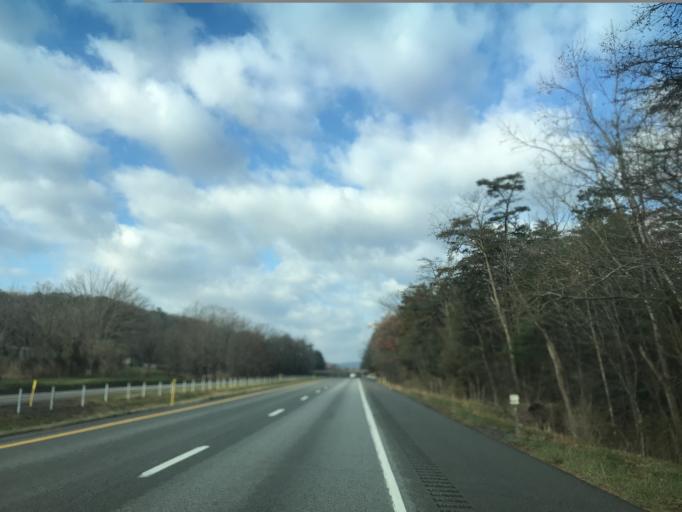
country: US
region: Maryland
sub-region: Washington County
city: Hancock
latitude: 39.7944
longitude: -78.2181
